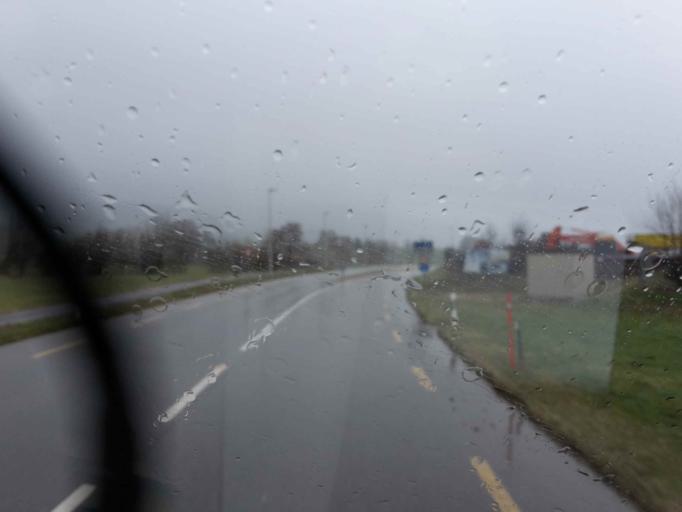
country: CH
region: Solothurn
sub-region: Bezirk Thal
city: Matzendorf
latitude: 47.2976
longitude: 7.6131
